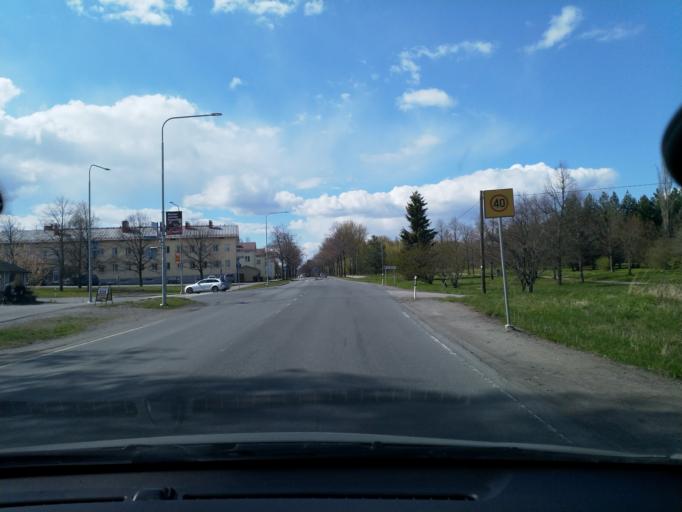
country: FI
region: Pirkanmaa
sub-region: Tampere
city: Tampere
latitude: 61.4827
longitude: 23.8040
